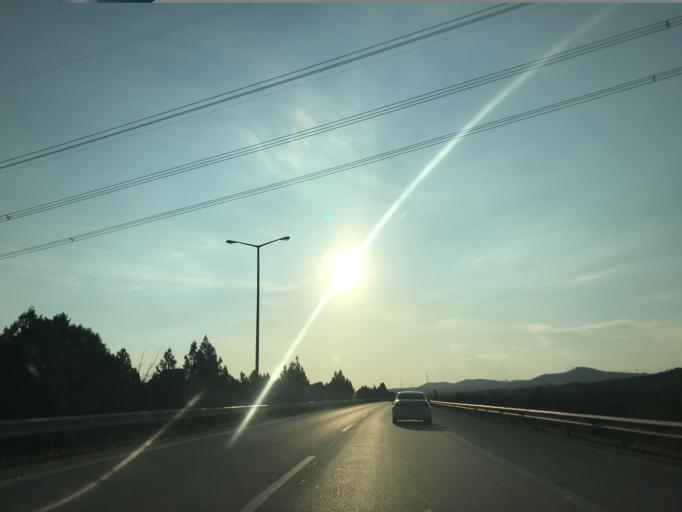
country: TR
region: Osmaniye
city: Toprakkale
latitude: 36.9683
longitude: 36.0514
